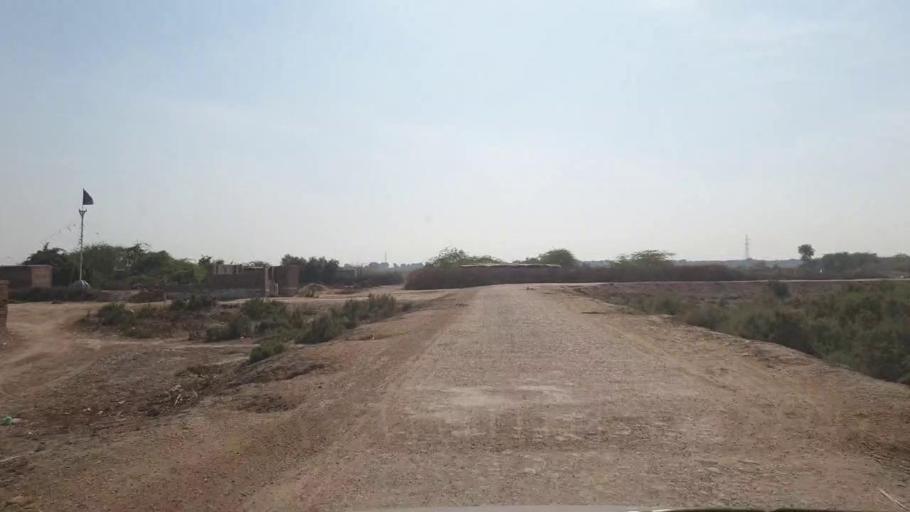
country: PK
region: Sindh
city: Chambar
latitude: 25.3326
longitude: 68.8047
